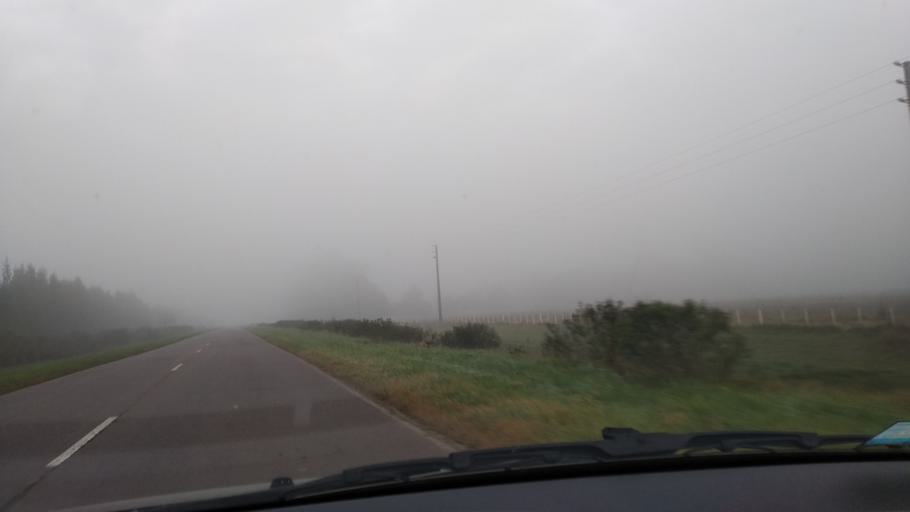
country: AR
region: Buenos Aires
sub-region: Partido de San Vicente
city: San Vicente
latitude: -35.2452
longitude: -58.4842
